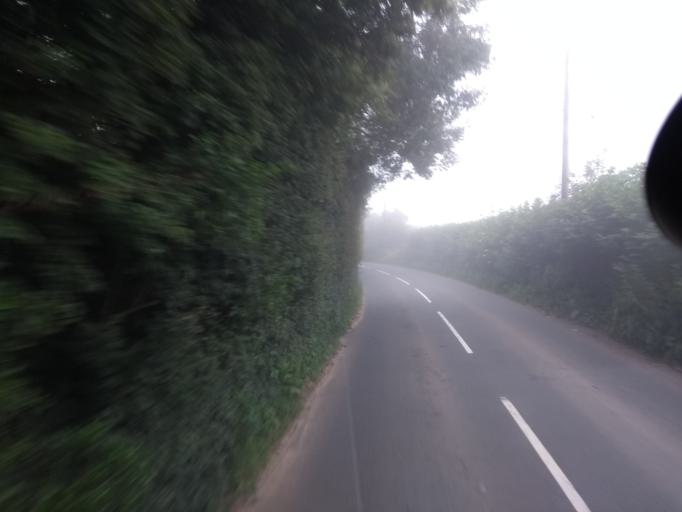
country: GB
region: England
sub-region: Dorset
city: Beaminster
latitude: 50.7879
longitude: -2.7885
